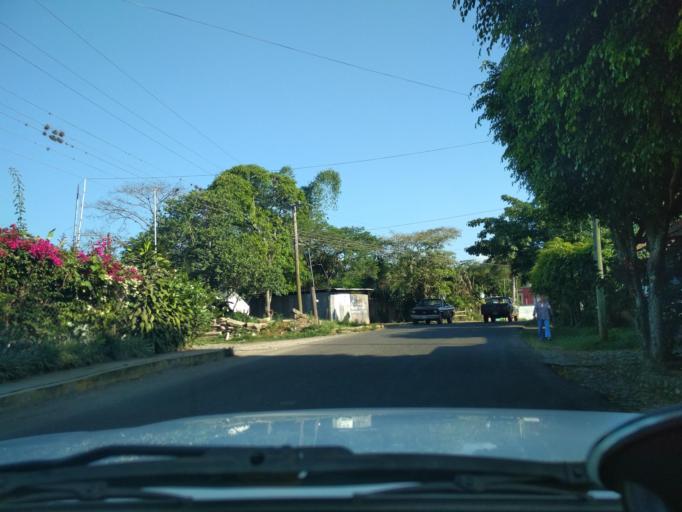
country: MX
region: Veracruz
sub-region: Fortin
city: Fraccionamiento Villas de la Llave
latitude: 18.9226
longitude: -96.9938
